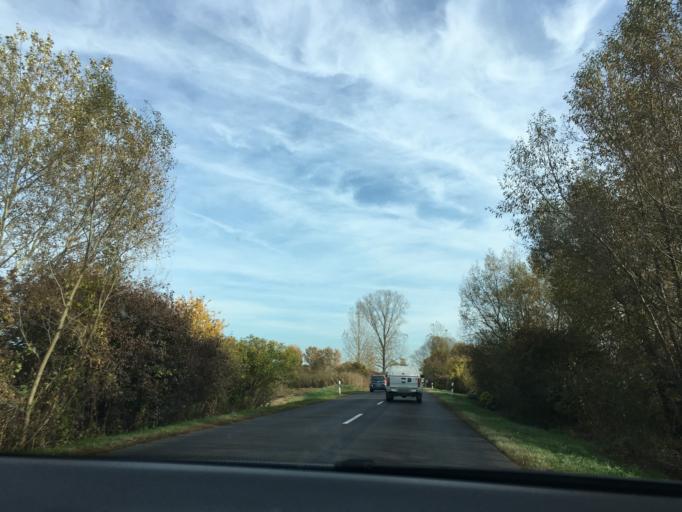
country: HU
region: Szabolcs-Szatmar-Bereg
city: Kisleta
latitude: 47.8552
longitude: 21.9859
